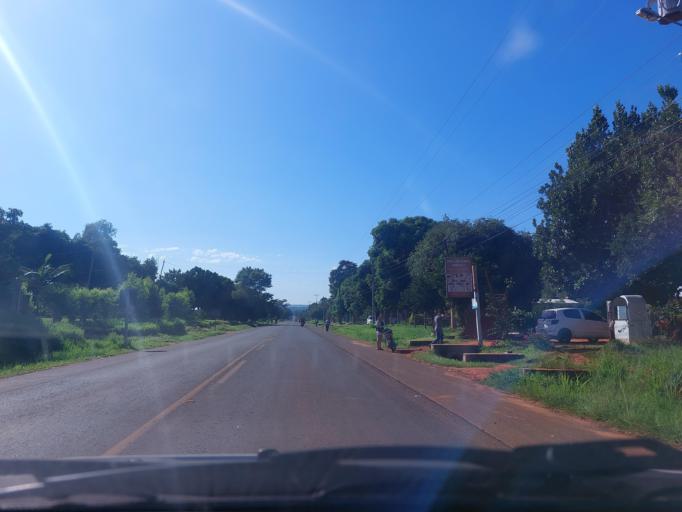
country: PY
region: San Pedro
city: Guayaybi
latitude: -24.5313
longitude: -56.4256
